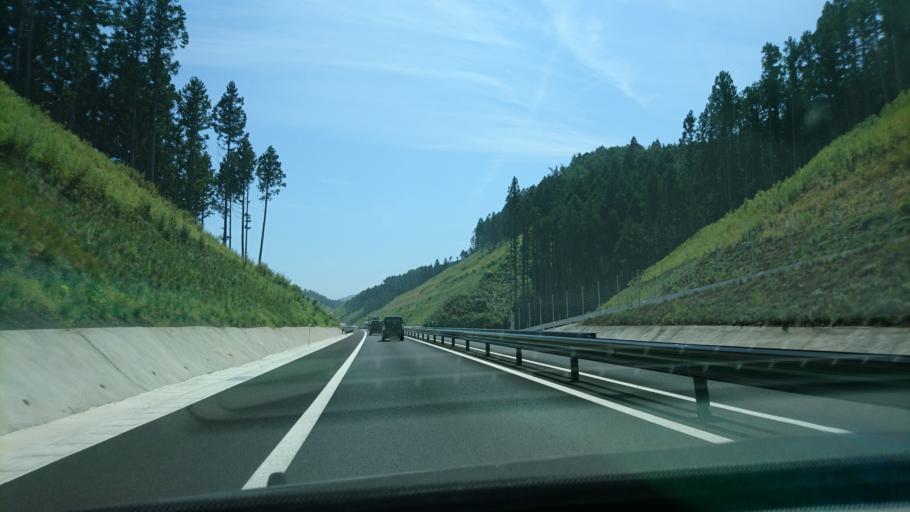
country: JP
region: Iwate
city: Ofunato
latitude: 39.0112
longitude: 141.6097
